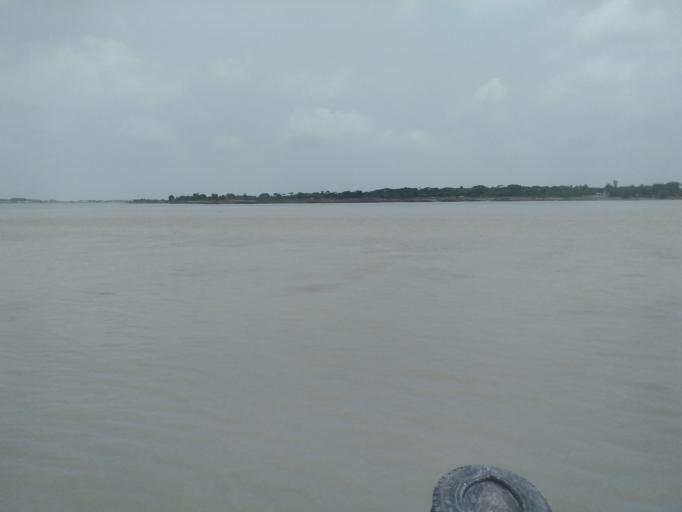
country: BD
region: Khulna
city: Phultala
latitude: 22.6421
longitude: 89.4133
